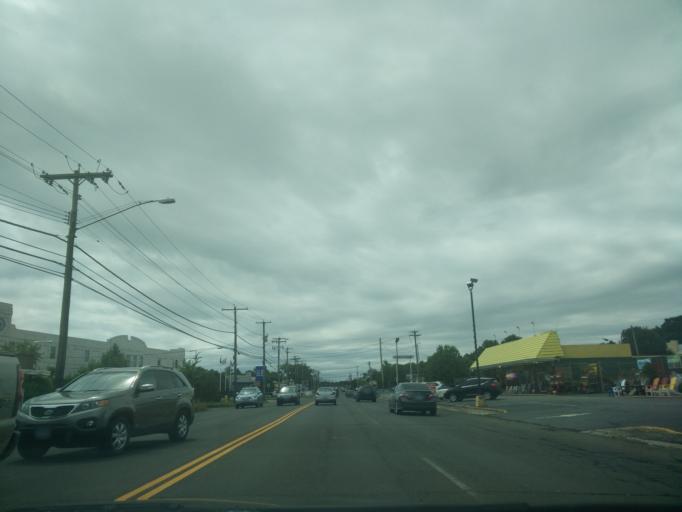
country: US
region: Connecticut
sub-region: New Haven County
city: Orange
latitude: 41.2450
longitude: -73.0284
